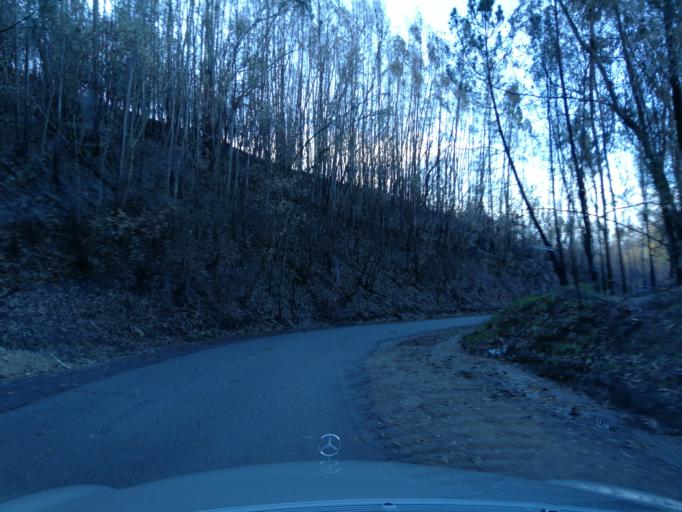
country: PT
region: Braga
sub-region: Braga
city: Braga
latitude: 41.5432
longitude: -8.3879
